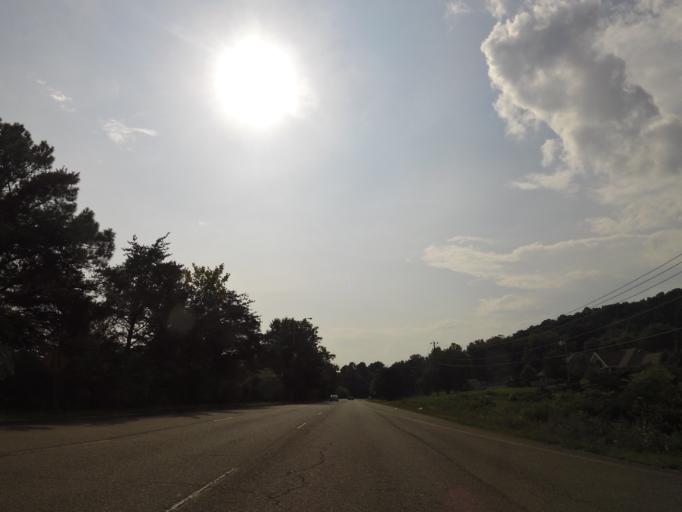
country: US
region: Tennessee
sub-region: Knox County
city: Knoxville
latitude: 36.0315
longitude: -83.8809
